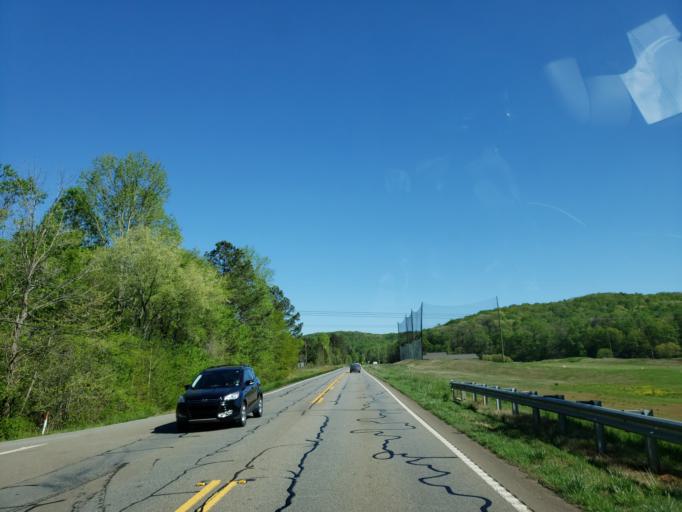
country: US
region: Georgia
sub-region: Cherokee County
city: Canton
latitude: 34.3044
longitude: -84.5259
